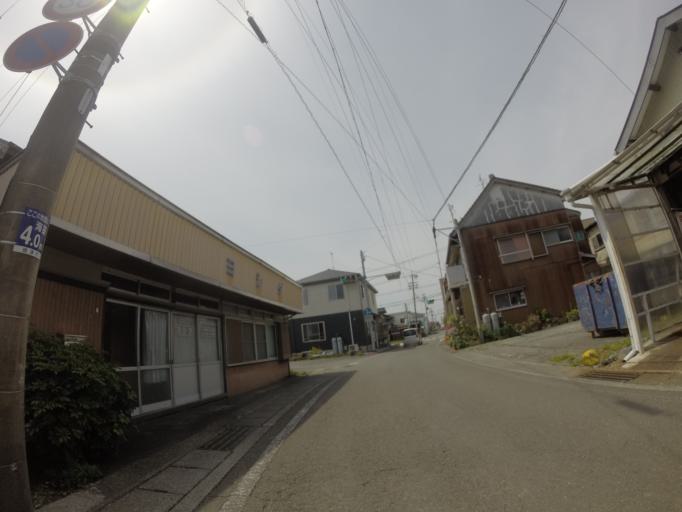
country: JP
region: Shizuoka
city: Yaizu
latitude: 34.7946
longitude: 138.2964
